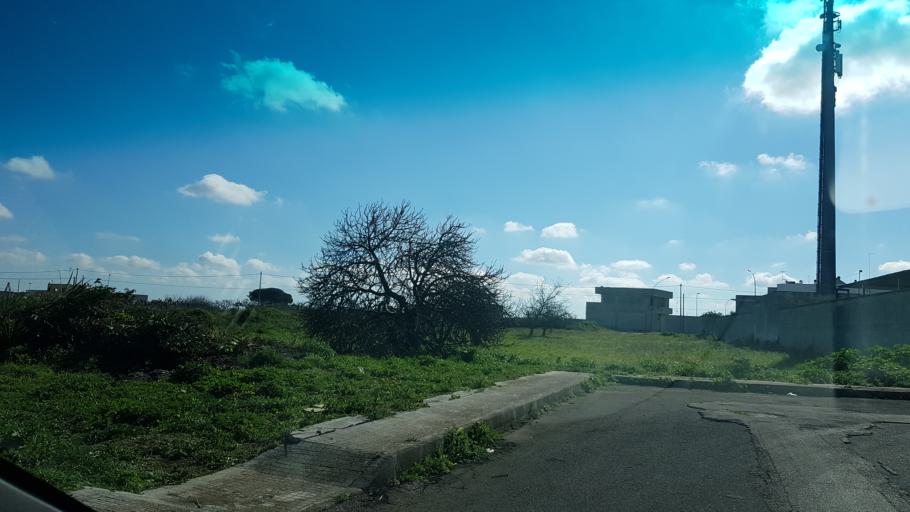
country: IT
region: Apulia
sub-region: Provincia di Lecce
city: Squinzano
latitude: 40.4364
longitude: 18.0517
